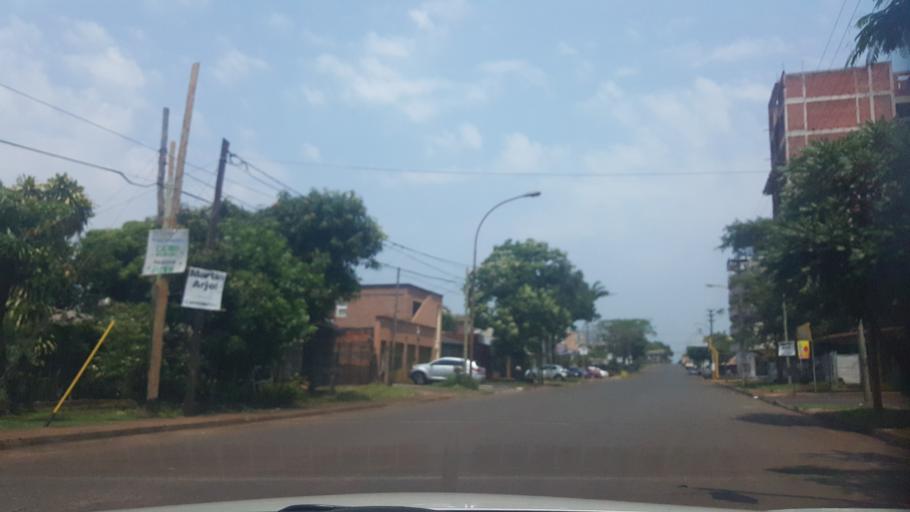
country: AR
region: Misiones
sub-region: Departamento de Capital
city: Posadas
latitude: -27.3873
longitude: -55.9042
